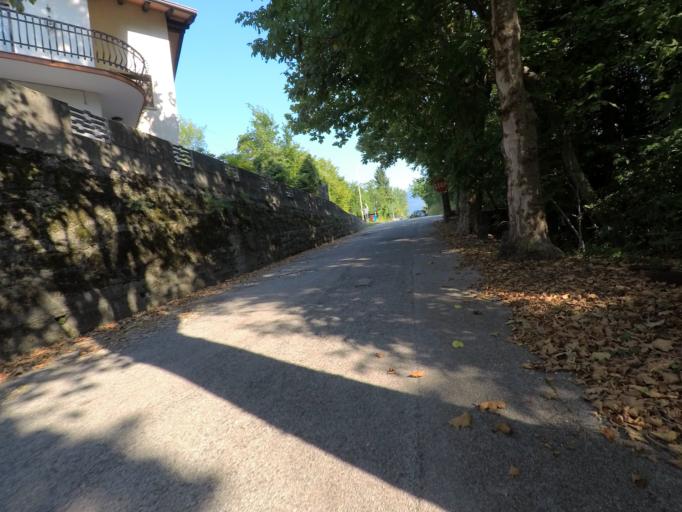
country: IT
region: Friuli Venezia Giulia
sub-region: Provincia di Pordenone
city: Pinzano al Tagliamento
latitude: 46.1818
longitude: 12.9515
